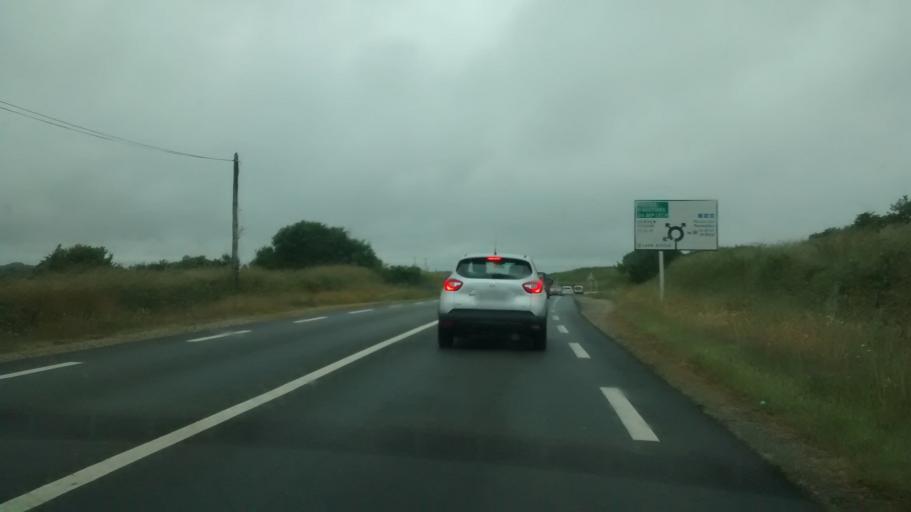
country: FR
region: Brittany
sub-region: Departement du Morbihan
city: Ploemeur
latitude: 47.7484
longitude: -3.4196
